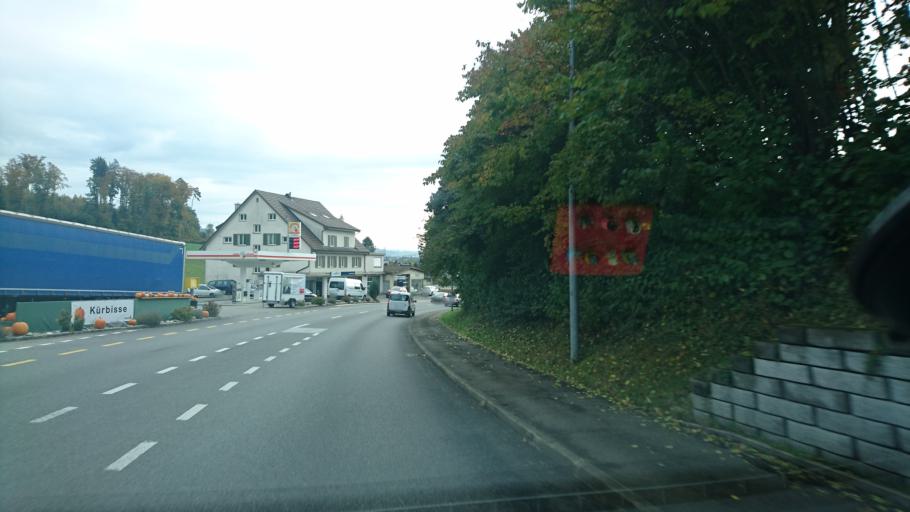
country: CH
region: Bern
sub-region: Bern-Mittelland District
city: Kirchlindach
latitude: 46.9776
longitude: 7.4204
